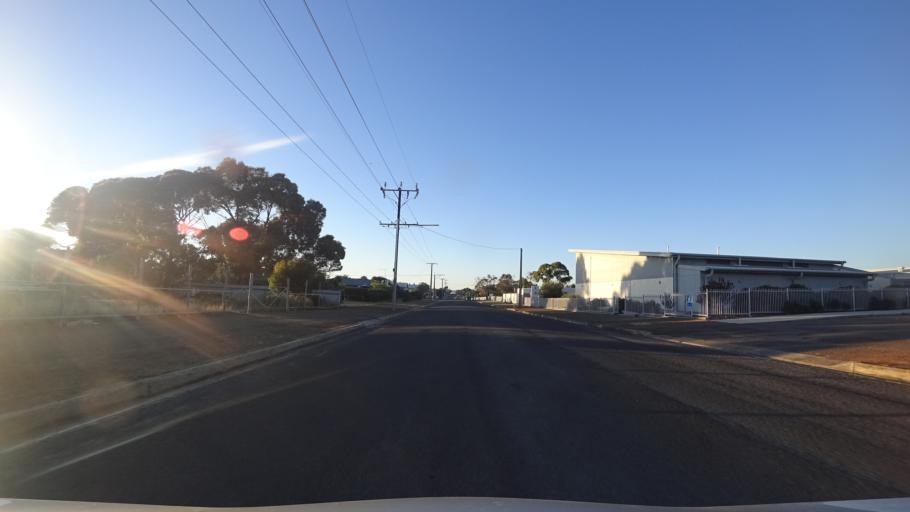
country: AU
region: South Australia
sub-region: Kangaroo Island
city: Kingscote
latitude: -35.6510
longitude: 137.6345
